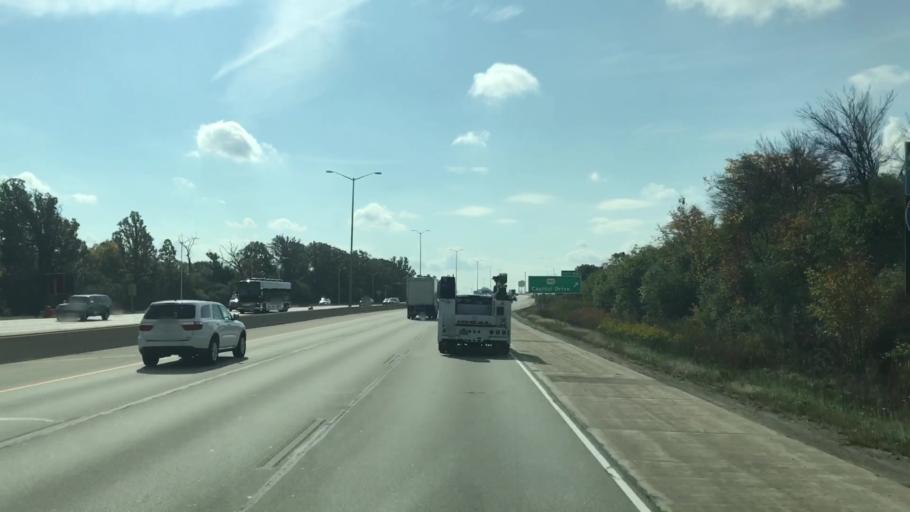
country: US
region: Wisconsin
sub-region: Waukesha County
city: Butler
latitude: 43.0947
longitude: -88.0584
